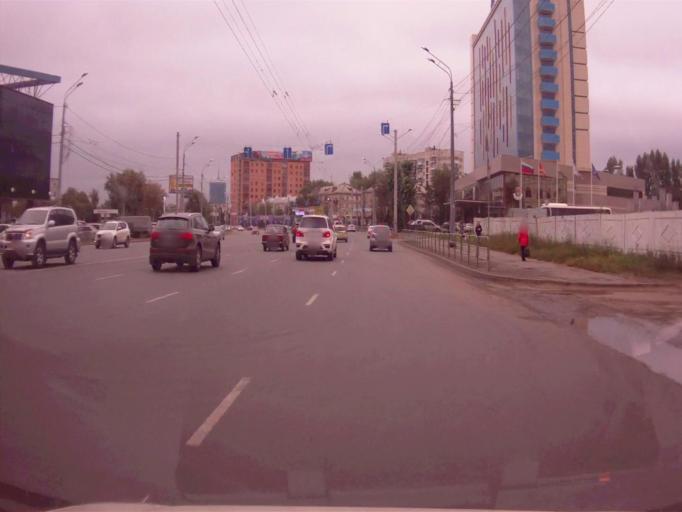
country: RU
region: Chelyabinsk
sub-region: Gorod Chelyabinsk
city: Chelyabinsk
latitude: 55.1653
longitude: 61.3805
